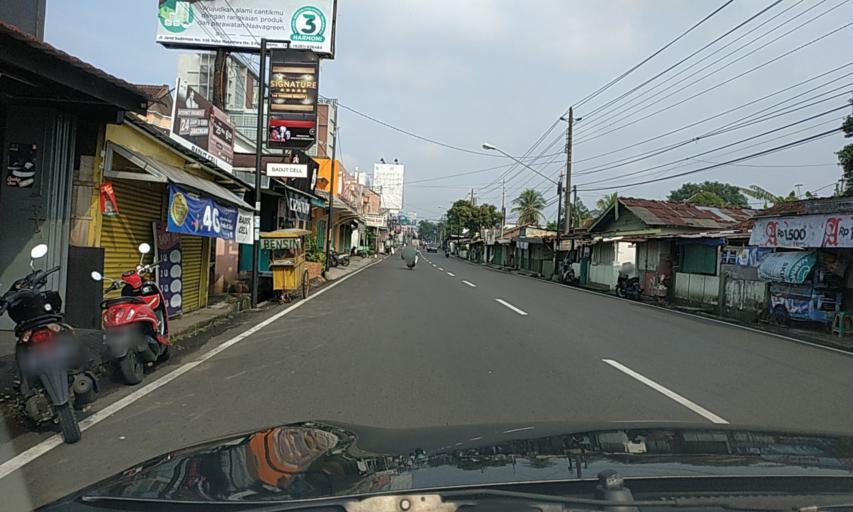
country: ID
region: Central Java
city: Purwokerto
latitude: -7.4171
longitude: 109.2466
